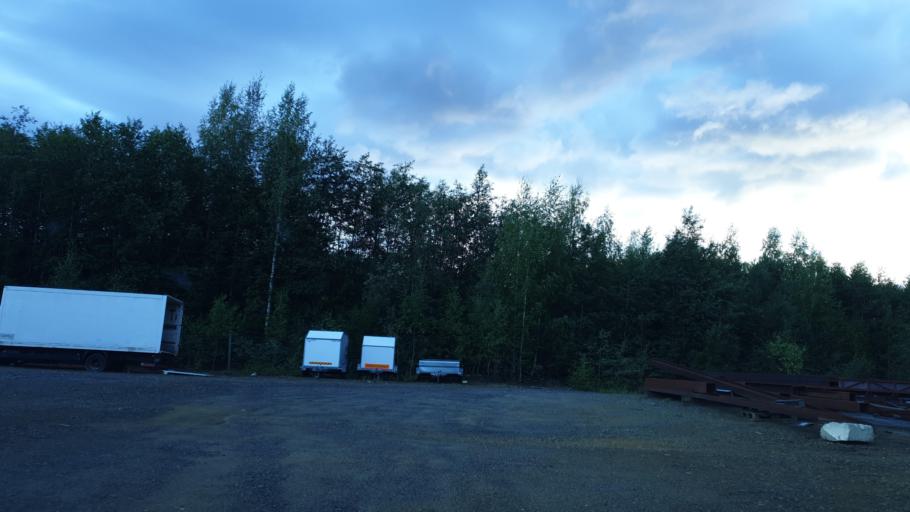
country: FI
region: Northern Savo
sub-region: Varkaus
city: Leppaevirta
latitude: 62.5795
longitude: 27.6095
